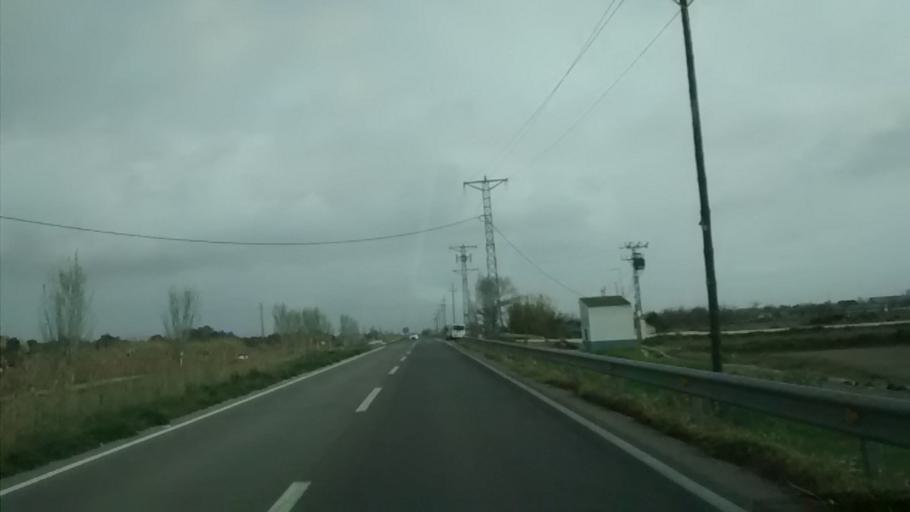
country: ES
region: Catalonia
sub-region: Provincia de Tarragona
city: Sant Carles de la Rapita
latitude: 40.6259
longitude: 0.6000
